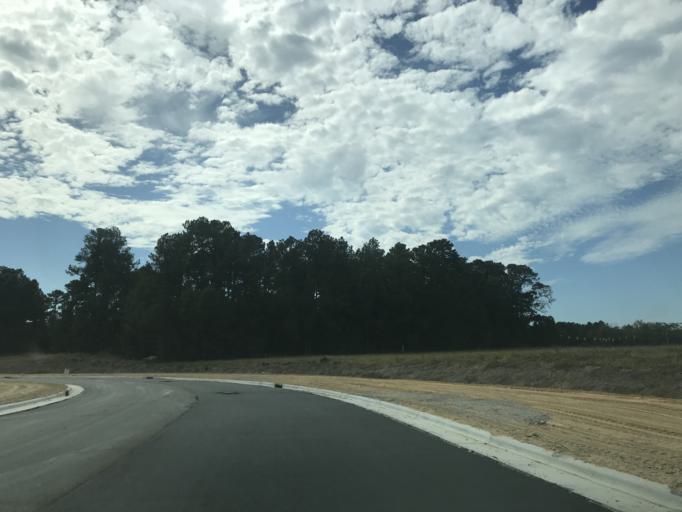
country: US
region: North Carolina
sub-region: Wake County
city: Knightdale
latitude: 35.8632
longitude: -78.5458
